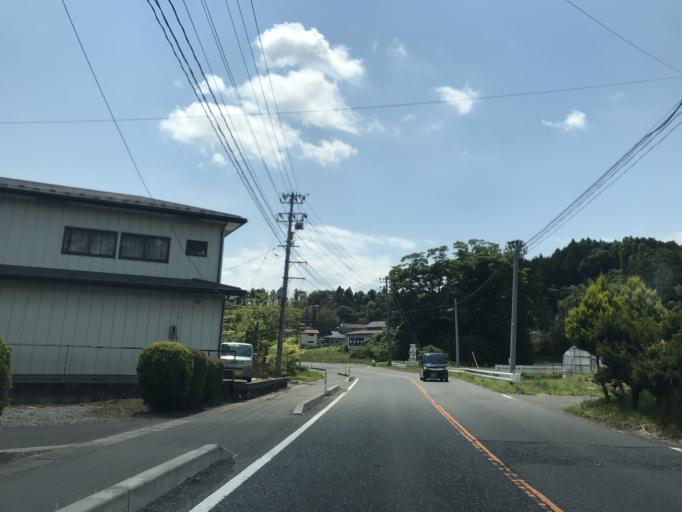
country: JP
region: Miyagi
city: Kogota
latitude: 38.5054
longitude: 141.0728
